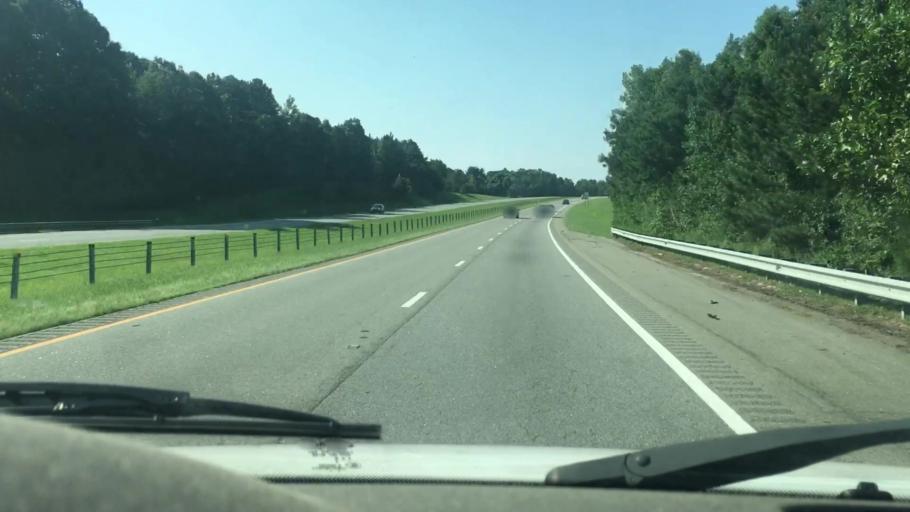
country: US
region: North Carolina
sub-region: Lincoln County
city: Lowesville
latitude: 35.3971
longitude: -80.9981
